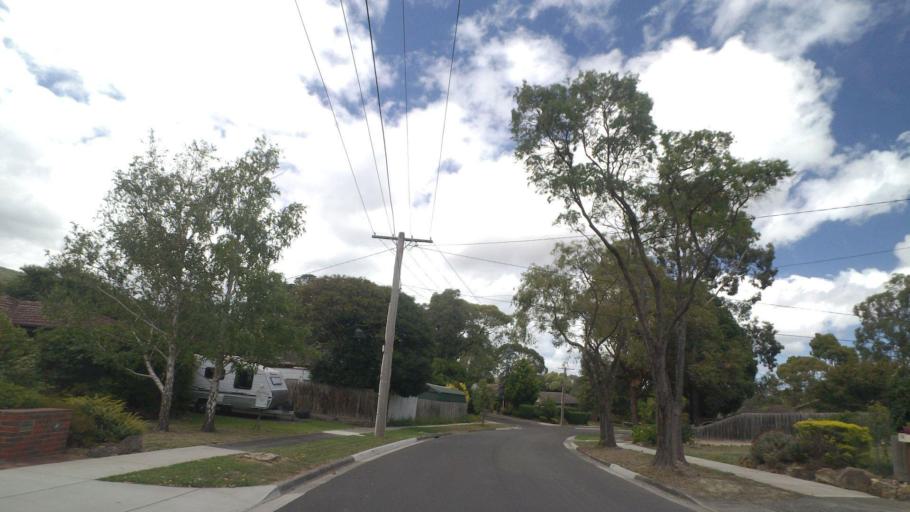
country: AU
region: Victoria
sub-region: Knox
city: Boronia
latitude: -37.8647
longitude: 145.2955
